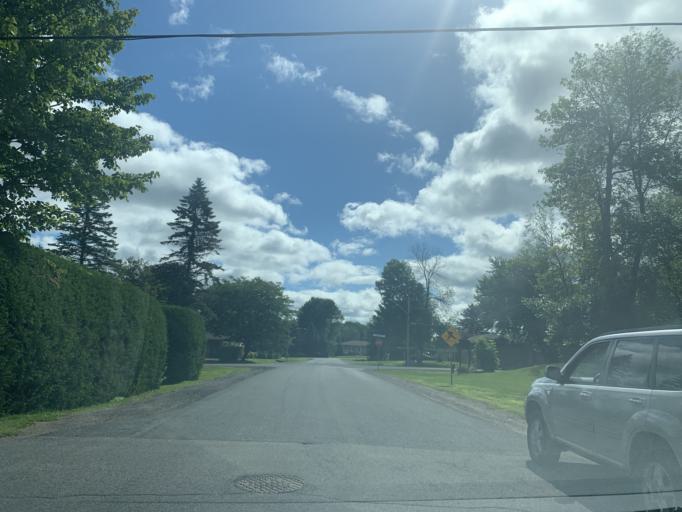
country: CA
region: Ontario
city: Hawkesbury
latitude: 45.6026
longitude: -74.5800
